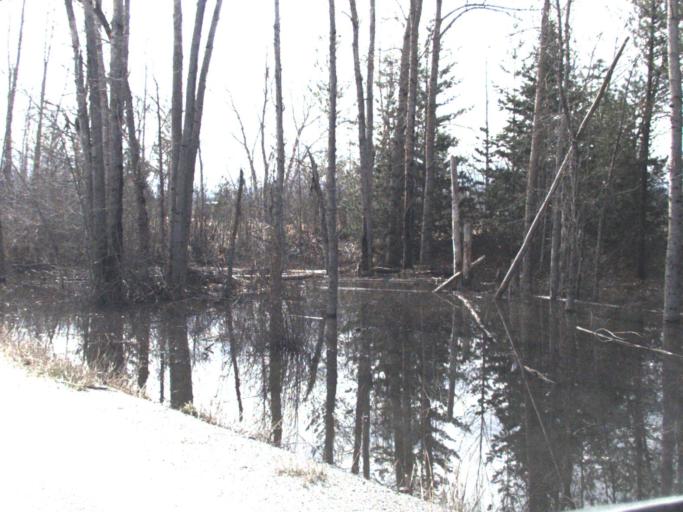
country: US
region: Washington
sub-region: Pend Oreille County
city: Newport
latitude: 48.3859
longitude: -117.3112
